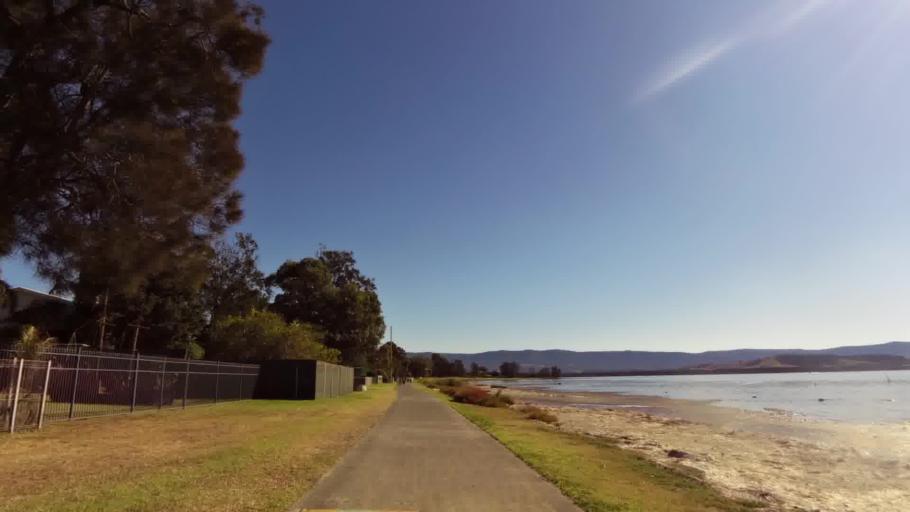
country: AU
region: New South Wales
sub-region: Shellharbour
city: Albion Park Rail
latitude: -34.5569
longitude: 150.8224
